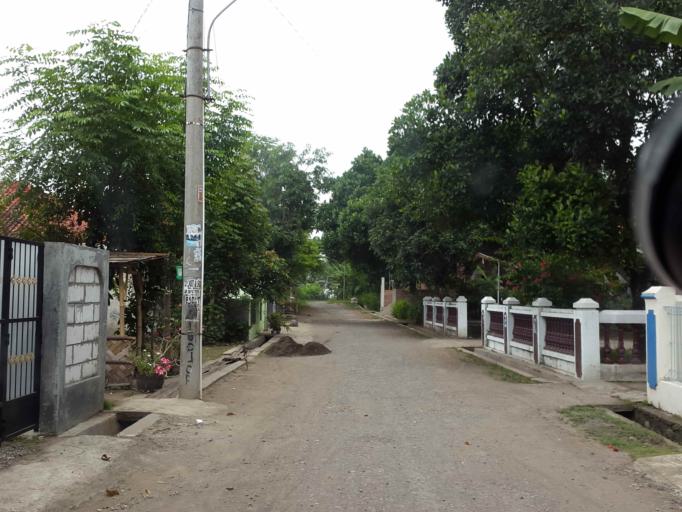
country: ID
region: Central Java
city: Pemalang
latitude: -6.9389
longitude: 109.3915
